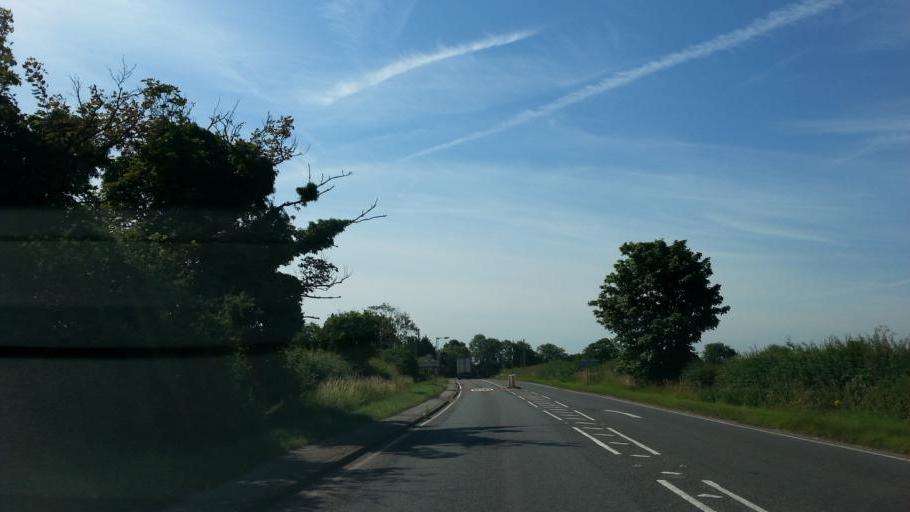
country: GB
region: England
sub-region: Nottinghamshire
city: Newark on Trent
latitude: 53.1107
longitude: -0.8203
